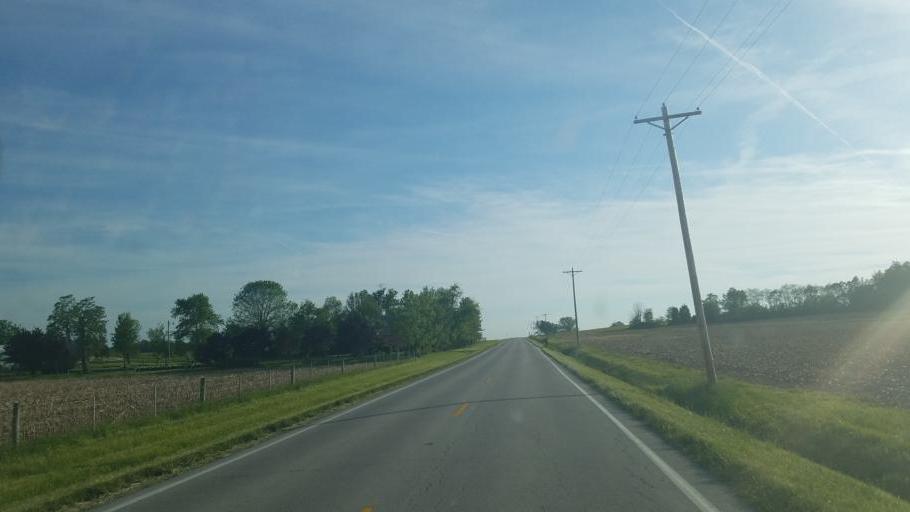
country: US
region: Ohio
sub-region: Highland County
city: Greenfield
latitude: 39.3974
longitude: -83.3175
